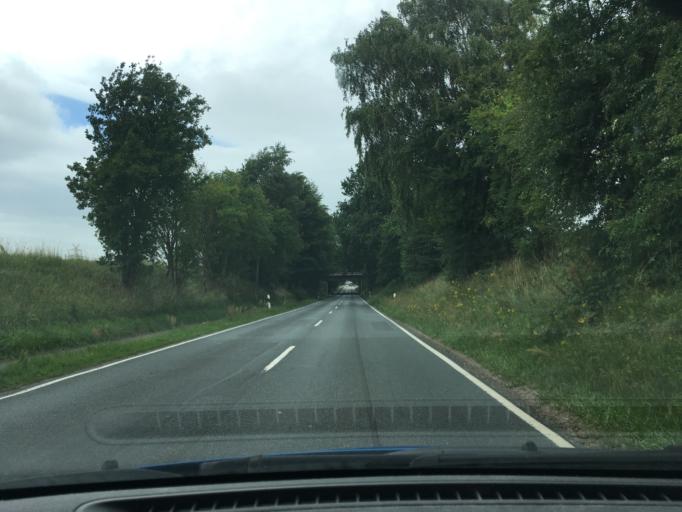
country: DE
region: Lower Saxony
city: Buchholz in der Nordheide
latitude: 53.3713
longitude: 9.9065
